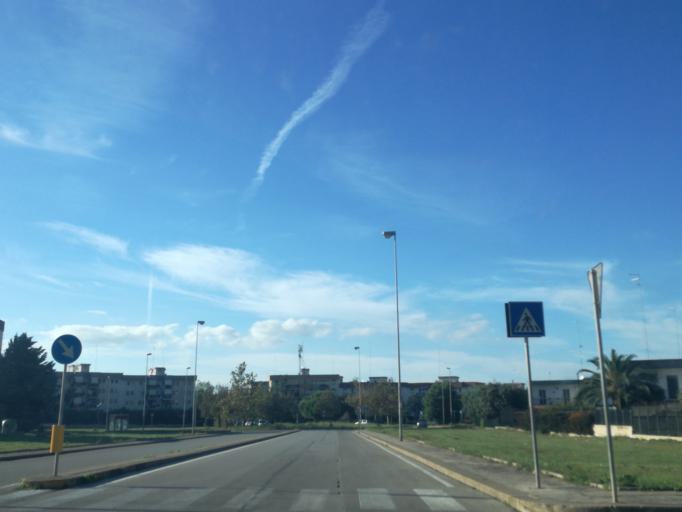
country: IT
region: Apulia
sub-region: Provincia di Bari
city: San Paolo
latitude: 41.1261
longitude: 16.7848
